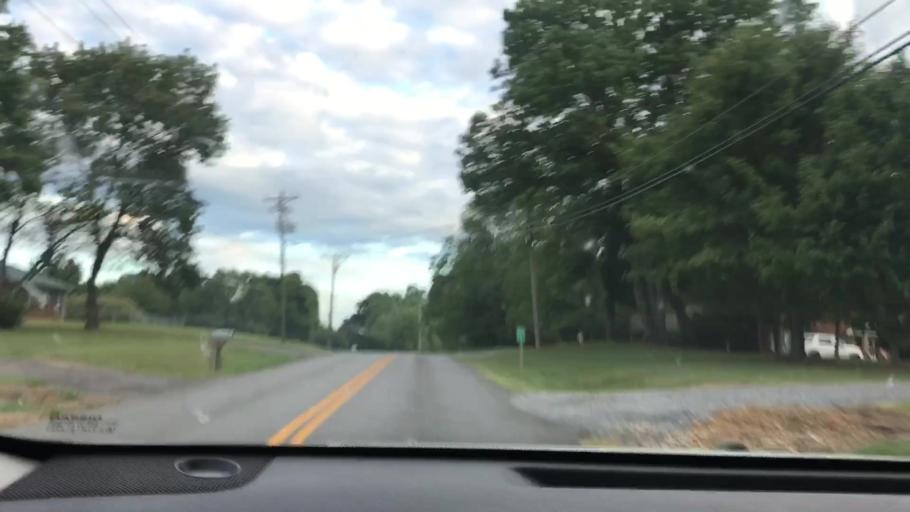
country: US
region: Kentucky
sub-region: Calloway County
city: Murray
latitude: 36.6316
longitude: -88.3030
